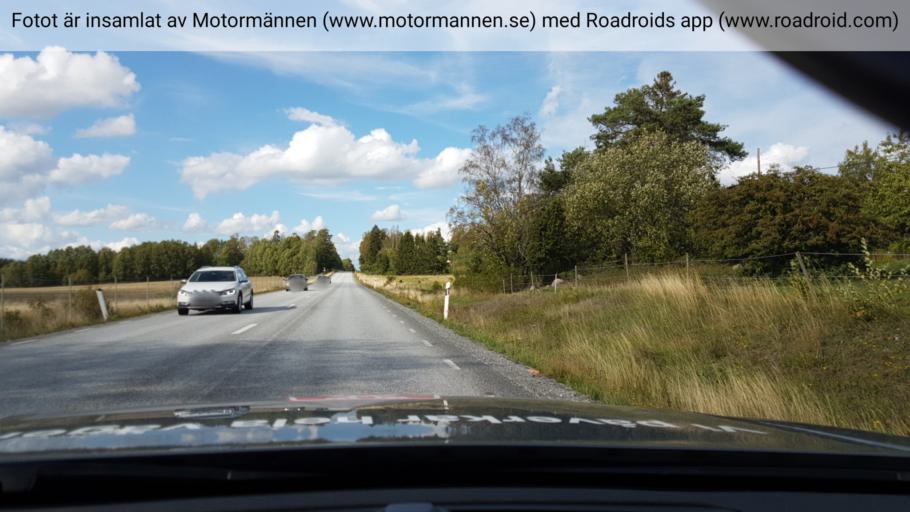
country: SE
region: Stockholm
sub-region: Upplands-Bro Kommun
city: Bro
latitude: 59.6020
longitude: 17.6103
